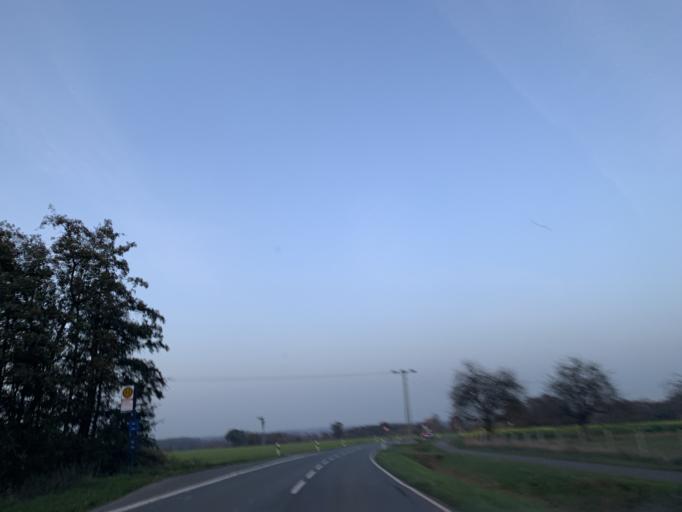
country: DE
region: North Rhine-Westphalia
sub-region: Regierungsbezirk Munster
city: Nottuln
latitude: 51.9789
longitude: 7.3550
